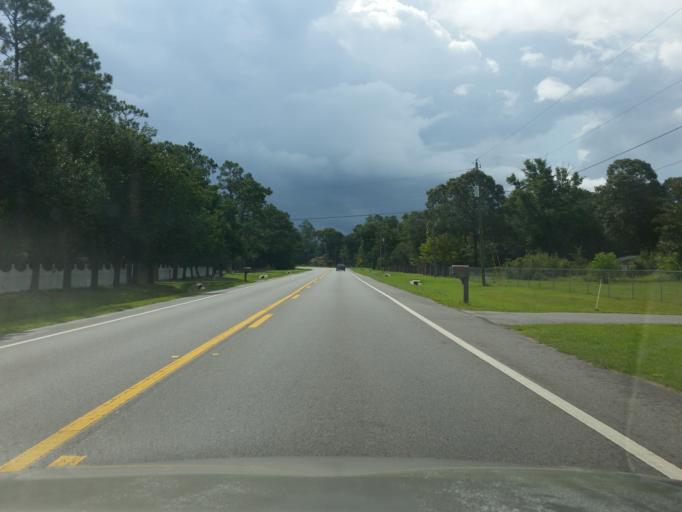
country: US
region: Florida
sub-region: Escambia County
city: Gonzalez
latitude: 30.5407
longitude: -87.3233
